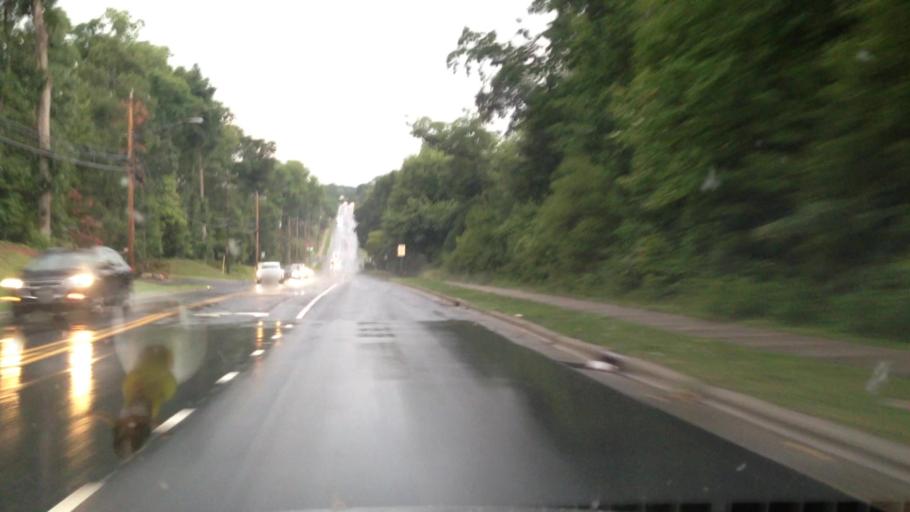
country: US
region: North Carolina
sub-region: Mecklenburg County
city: Pineville
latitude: 35.1361
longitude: -80.8893
